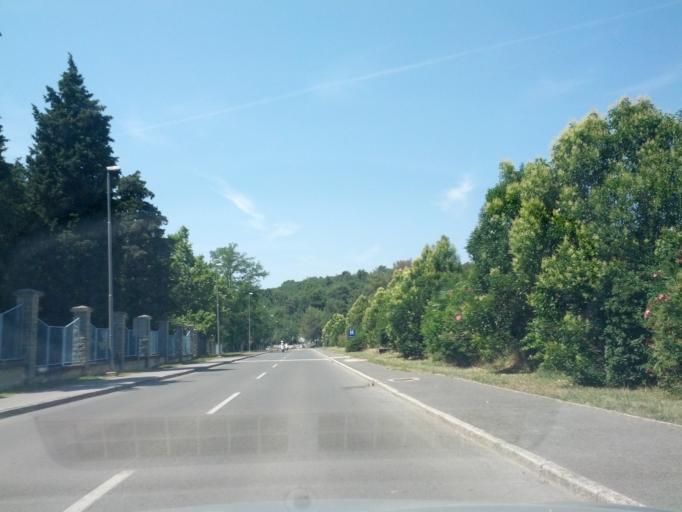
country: SI
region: Koper-Capodistria
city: Ankaran
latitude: 45.5806
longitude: 13.7305
